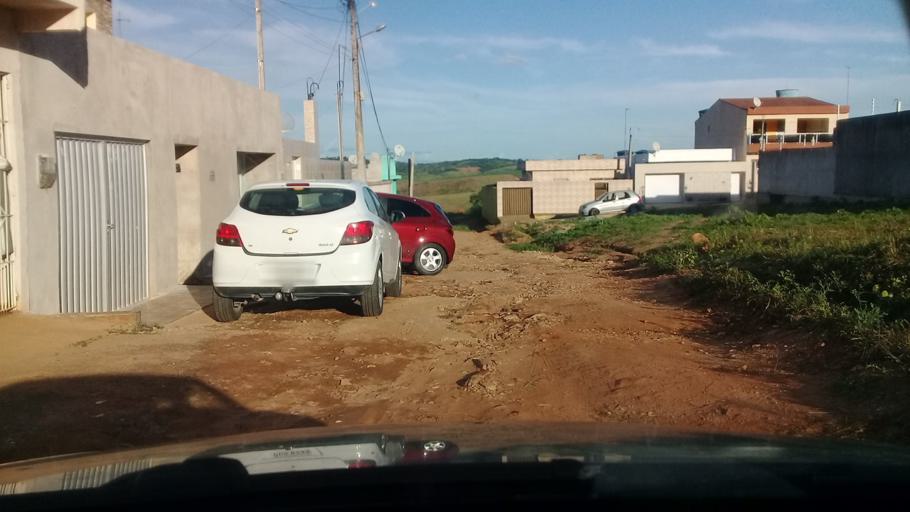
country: BR
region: Pernambuco
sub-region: Vicencia
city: Vicencia
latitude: -7.6090
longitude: -35.2290
